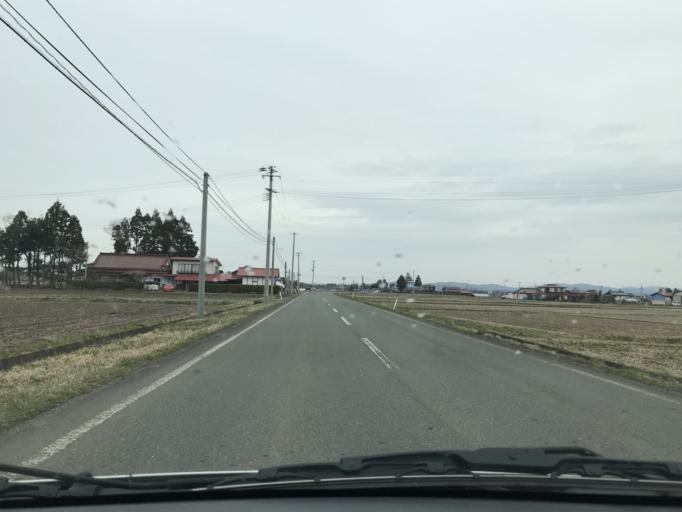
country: JP
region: Iwate
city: Mizusawa
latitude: 39.1690
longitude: 141.1112
